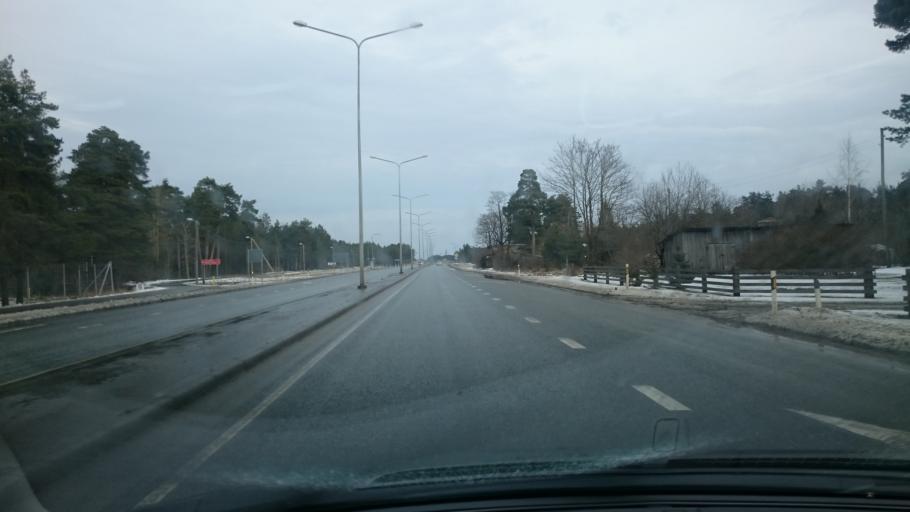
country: EE
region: Harju
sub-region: Saku vald
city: Saku
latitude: 59.3369
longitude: 24.6994
